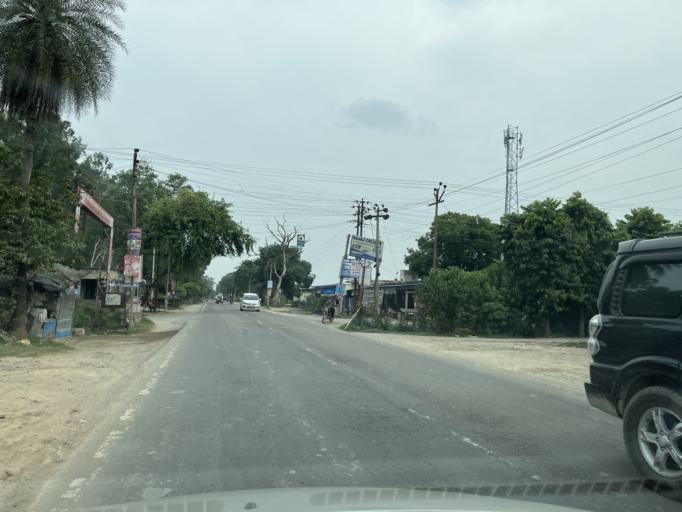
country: IN
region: Uttar Pradesh
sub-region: Rampur
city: Bilaspur
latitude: 29.0316
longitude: 79.2617
